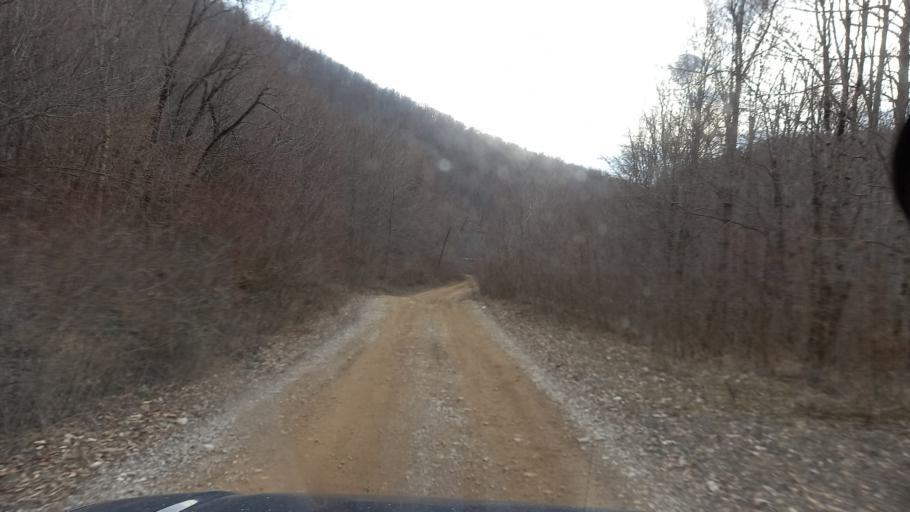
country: RU
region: Adygeya
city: Kamennomostskiy
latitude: 44.1670
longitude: 40.2994
